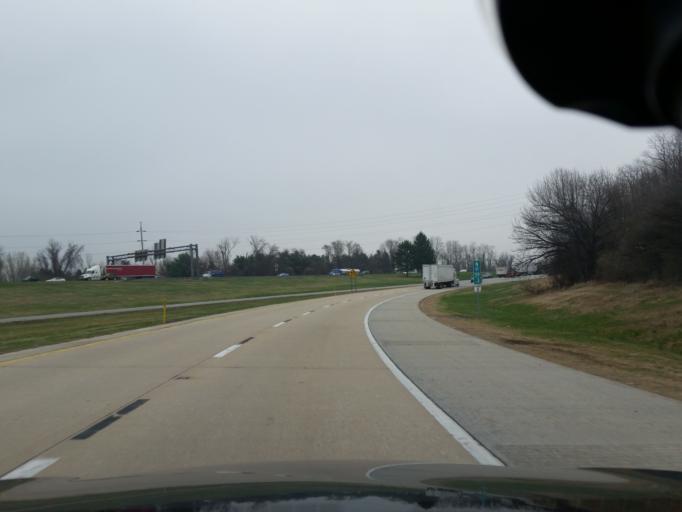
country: US
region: Pennsylvania
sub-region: Cumberland County
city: Mechanicsburg
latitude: 40.2741
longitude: -76.9988
